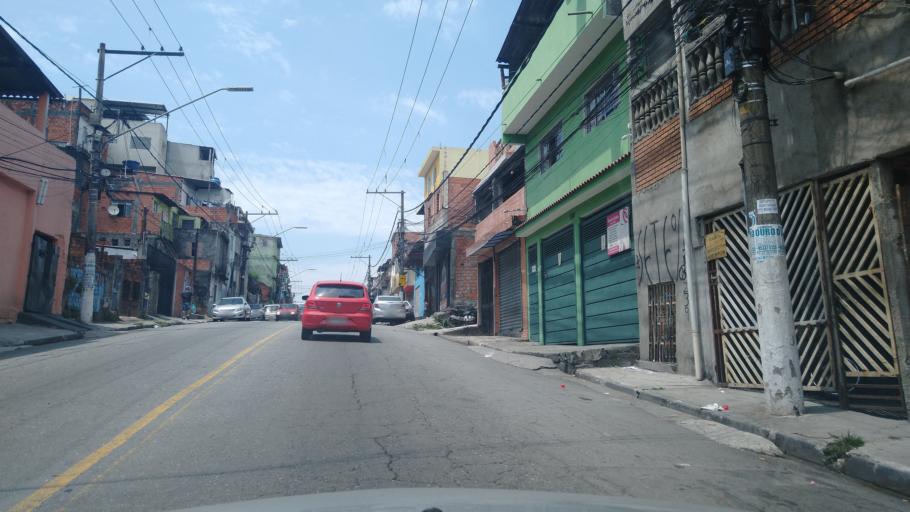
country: BR
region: Sao Paulo
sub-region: Sao Paulo
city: Sao Paulo
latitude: -23.4573
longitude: -46.6909
